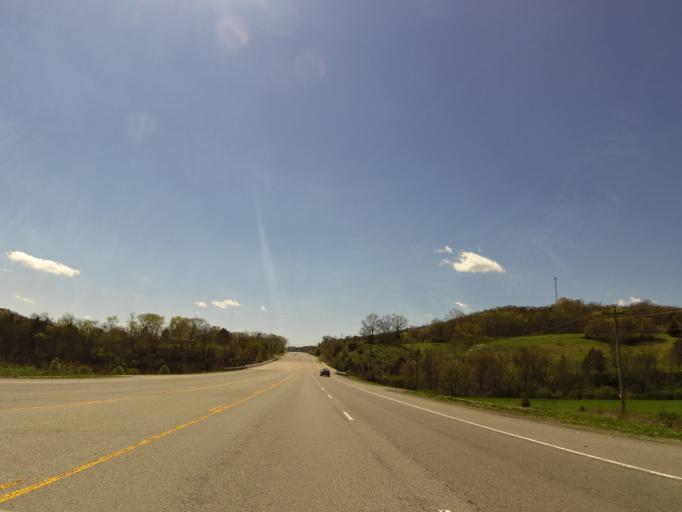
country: US
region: Tennessee
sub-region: DeKalb County
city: Smithville
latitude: 36.0110
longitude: -85.9641
